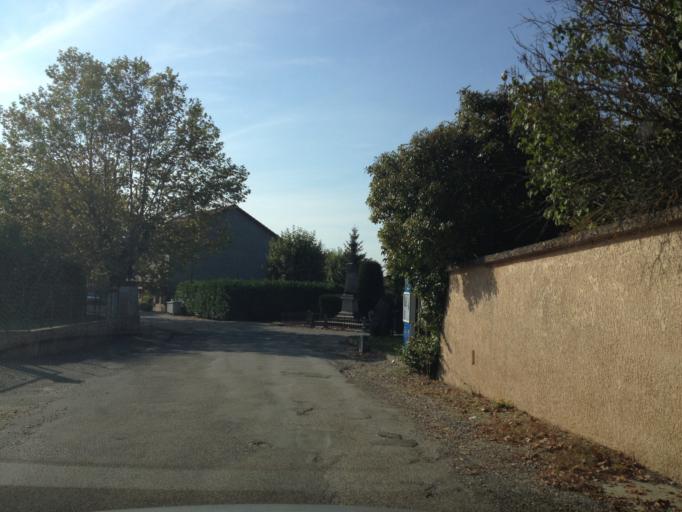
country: FR
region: Rhone-Alpes
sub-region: Departement de l'Isere
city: Bonnefamille
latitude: 45.5967
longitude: 5.1308
